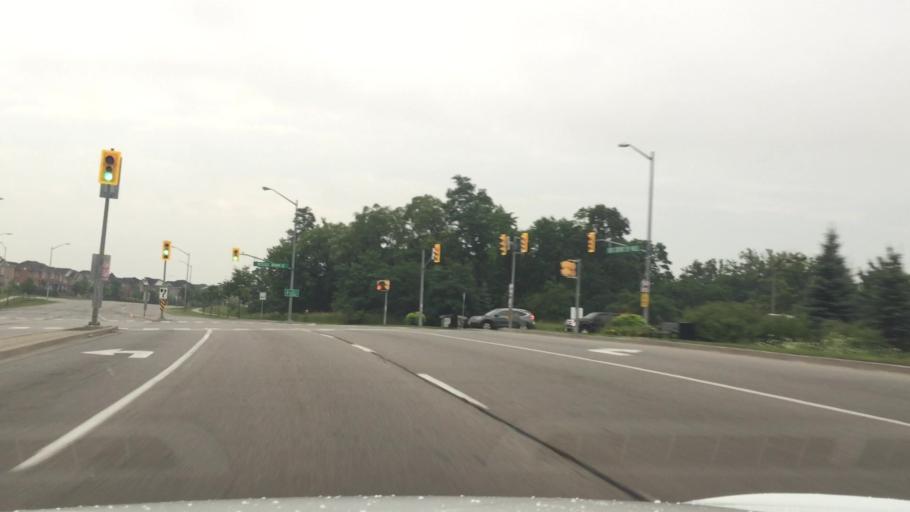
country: CA
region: Ontario
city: Markham
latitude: 43.8654
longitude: -79.2299
